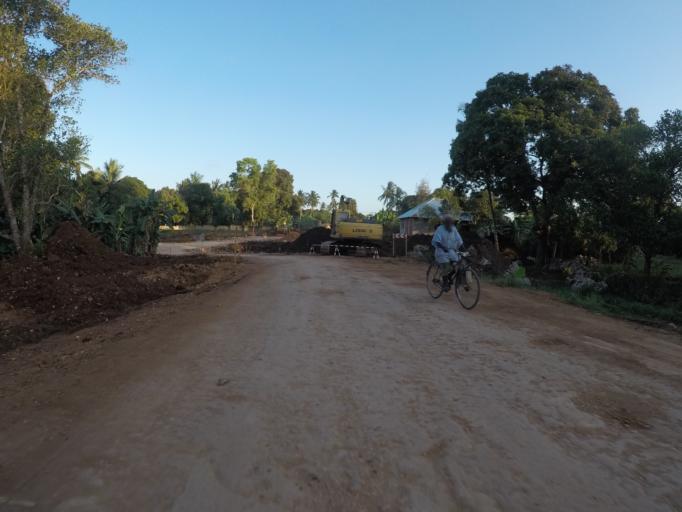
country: TZ
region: Zanzibar North
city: Gamba
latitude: -5.9182
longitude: 39.2994
